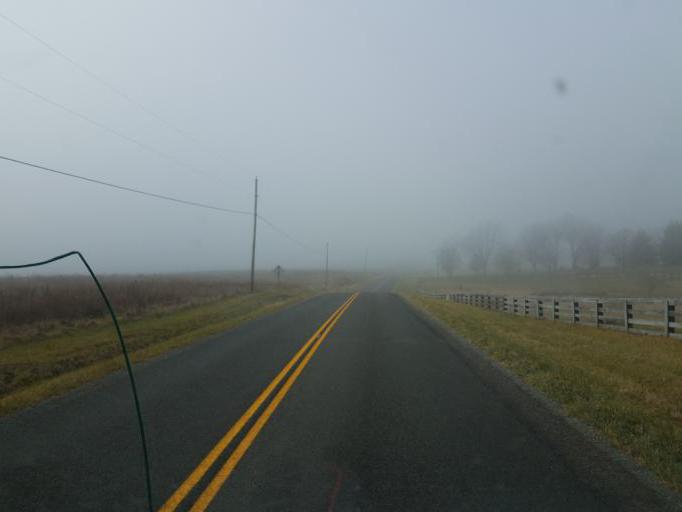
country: US
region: Ohio
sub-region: Champaign County
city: North Lewisburg
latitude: 40.3067
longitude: -83.6141
